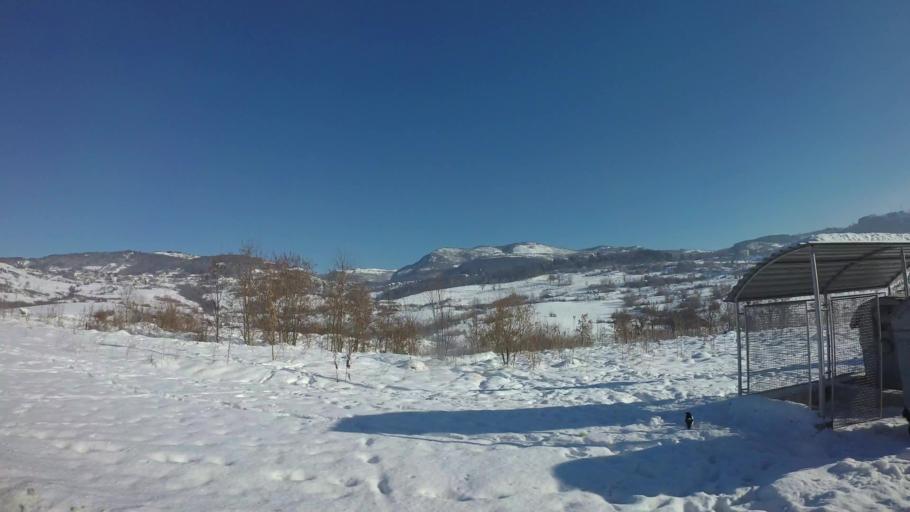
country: BA
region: Federation of Bosnia and Herzegovina
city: Kobilja Glava
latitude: 43.8819
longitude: 18.3974
